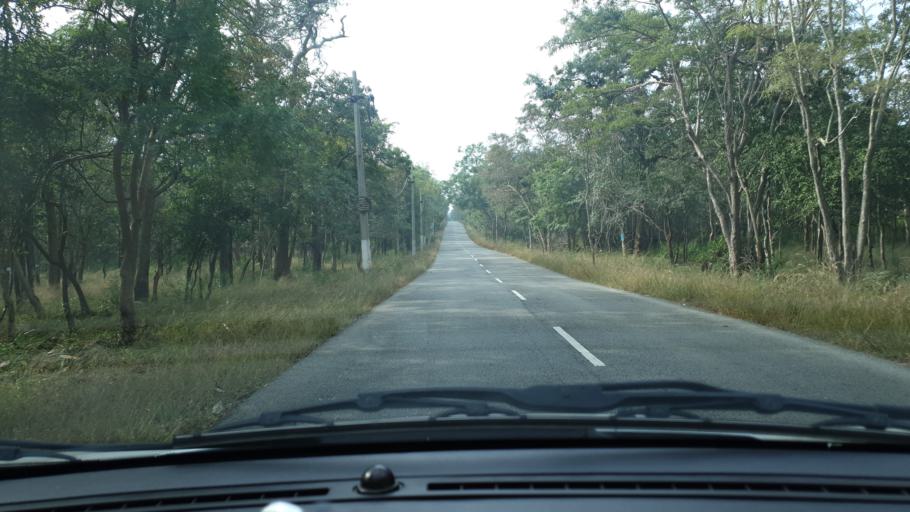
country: IN
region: Andhra Pradesh
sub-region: Kurnool
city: Srisailam
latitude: 16.2896
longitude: 78.7296
